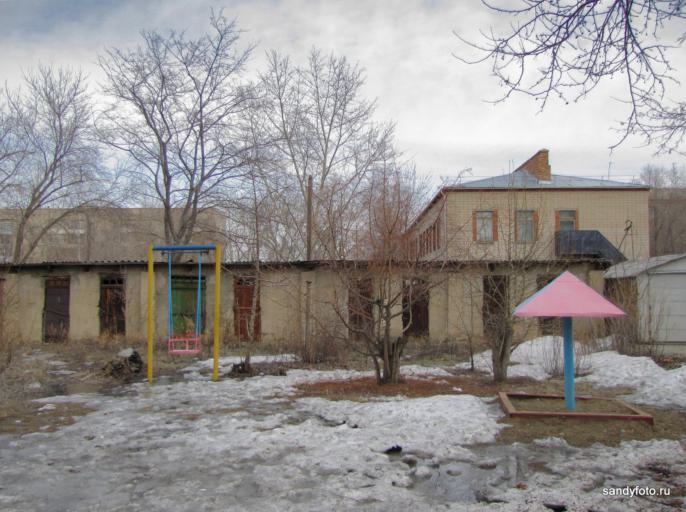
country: RU
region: Chelyabinsk
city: Troitsk
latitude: 54.1039
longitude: 61.5581
